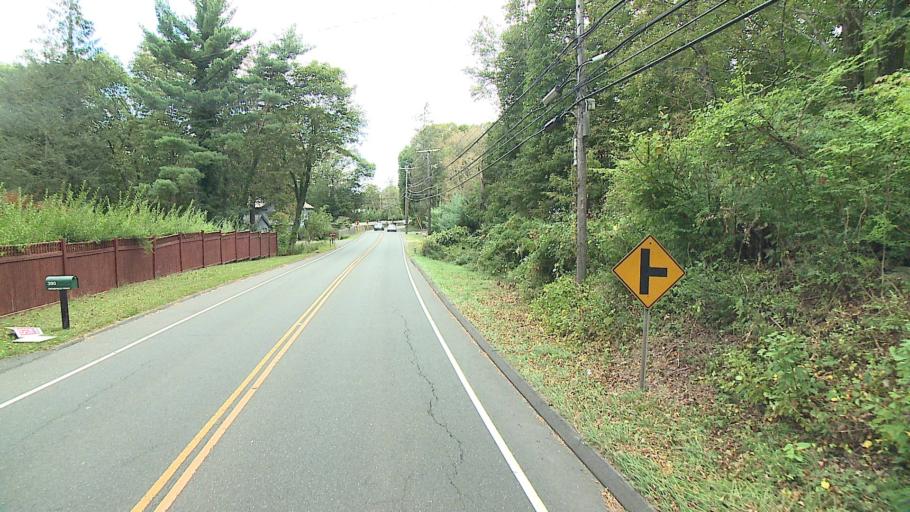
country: US
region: Connecticut
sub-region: Fairfield County
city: Wilton
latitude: 41.2094
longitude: -73.4573
